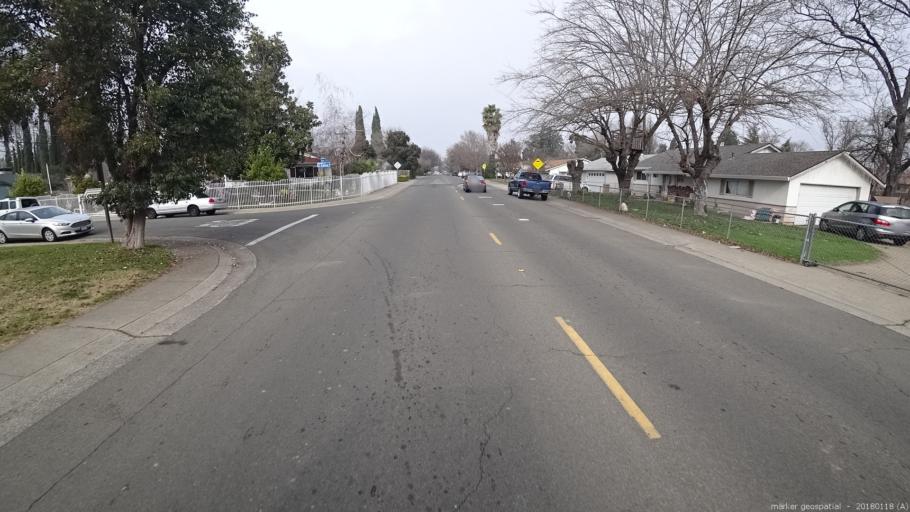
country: US
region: California
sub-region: Sacramento County
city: Rancho Cordova
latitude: 38.5934
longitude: -121.3090
